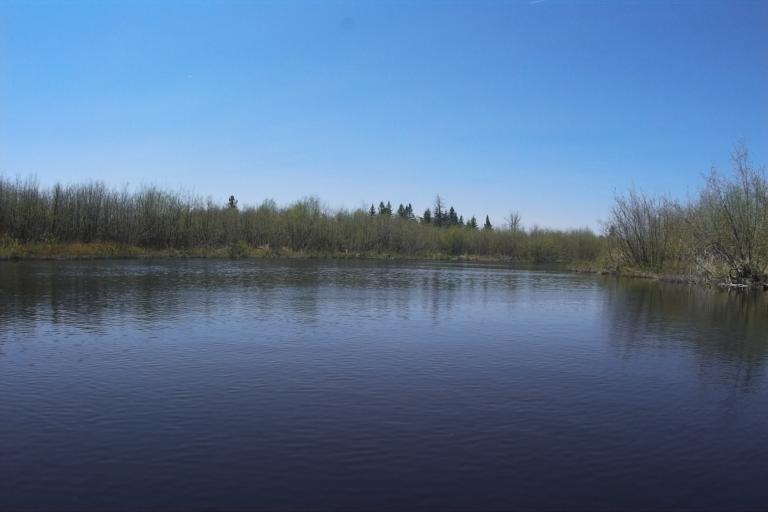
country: CA
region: Ontario
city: Powassan
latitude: 46.1592
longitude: -79.2555
